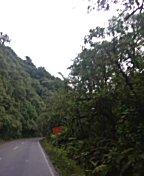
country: CR
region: San Jose
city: Dulce Nombre de Jesus
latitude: 10.0734
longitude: -83.9820
